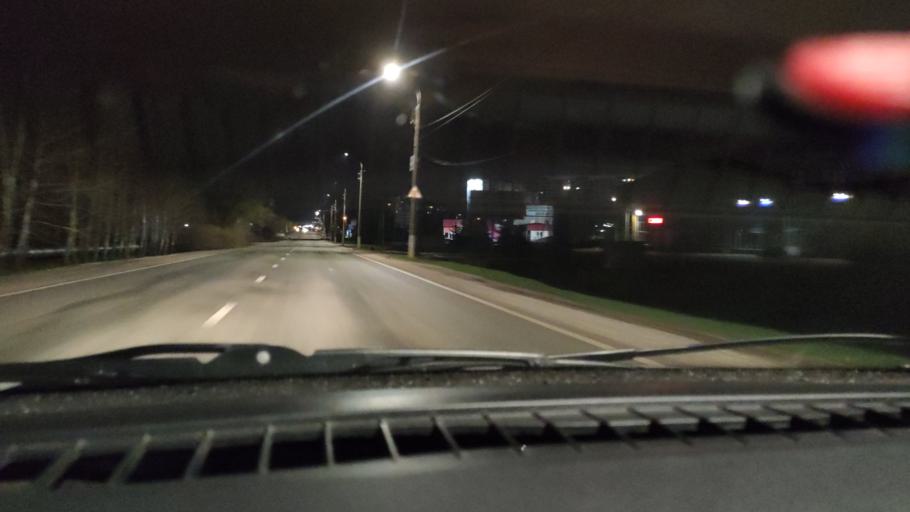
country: RU
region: Bashkortostan
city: Sterlitamak
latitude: 53.6437
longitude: 55.8924
